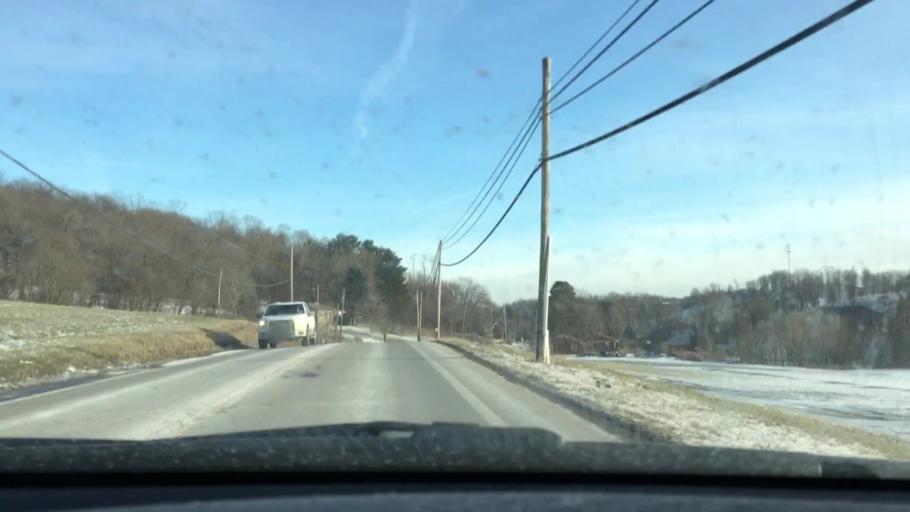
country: US
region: Pennsylvania
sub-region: Washington County
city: Gastonville
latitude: 40.2759
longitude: -80.0276
